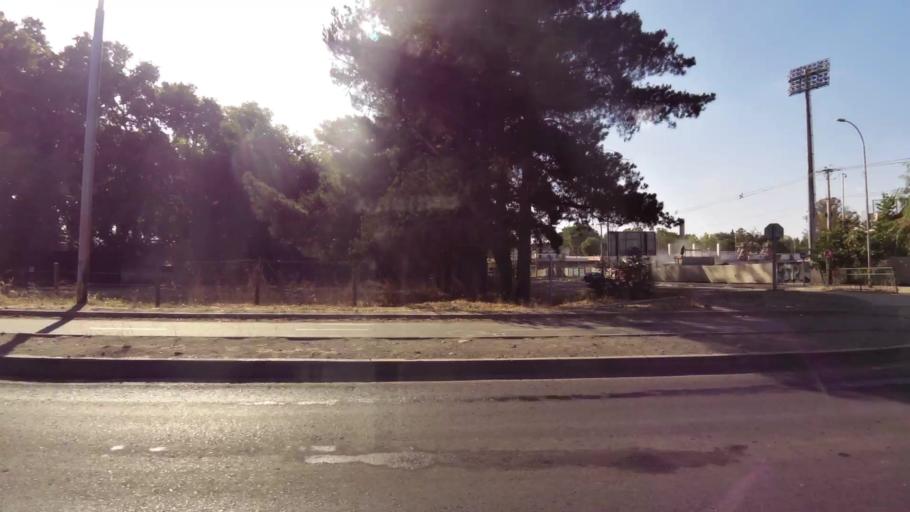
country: CL
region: Maule
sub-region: Provincia de Talca
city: Talca
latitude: -35.4185
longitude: -71.6745
